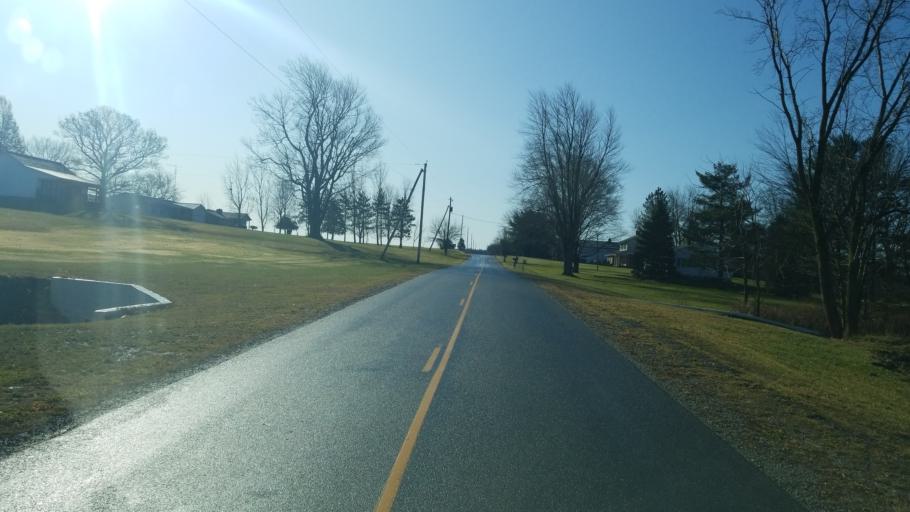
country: US
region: Ohio
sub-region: Richland County
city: Shelby
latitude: 40.8408
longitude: -82.6775
